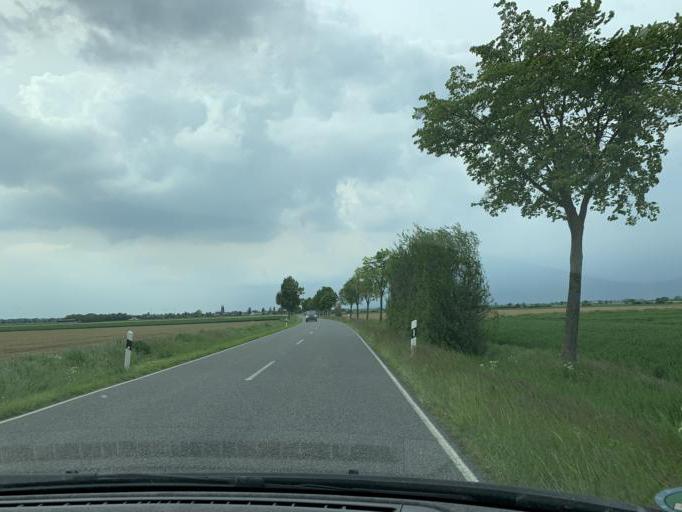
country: DE
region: North Rhine-Westphalia
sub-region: Regierungsbezirk Koln
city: Vettweiss
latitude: 50.7522
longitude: 6.5748
